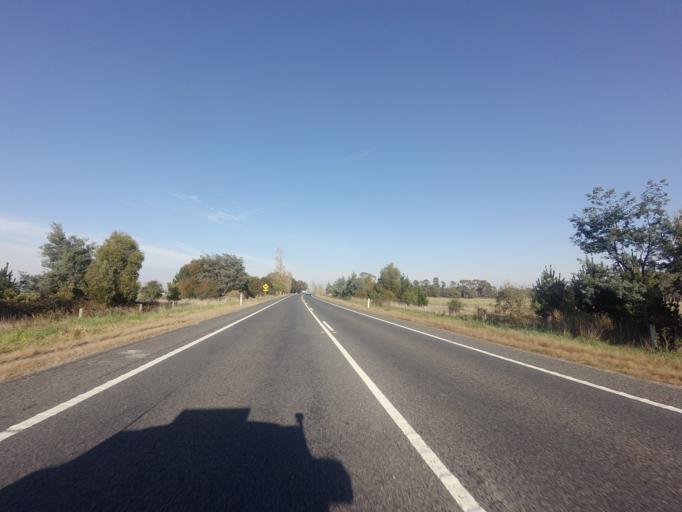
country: AU
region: Tasmania
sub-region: Northern Midlands
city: Longford
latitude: -41.5800
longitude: 147.1361
